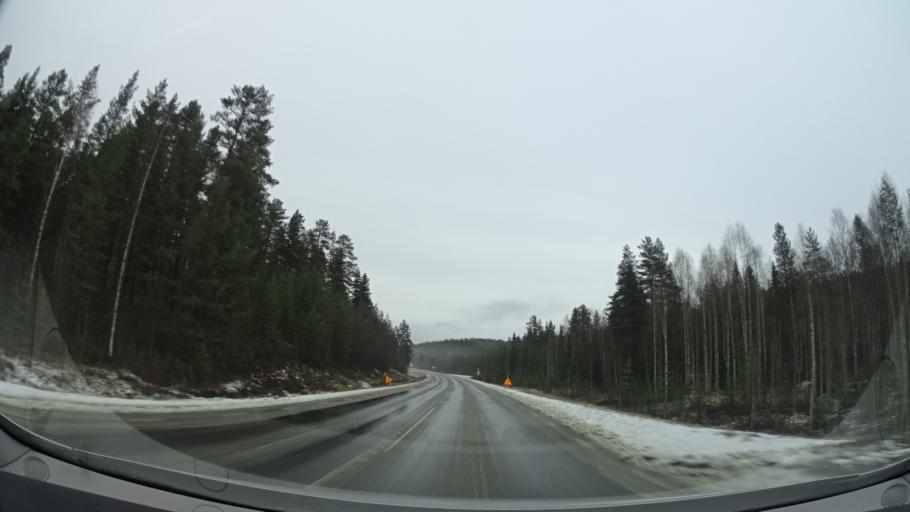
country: SE
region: Vaesterbotten
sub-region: Lycksele Kommun
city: Lycksele
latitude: 64.5759
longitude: 18.6526
